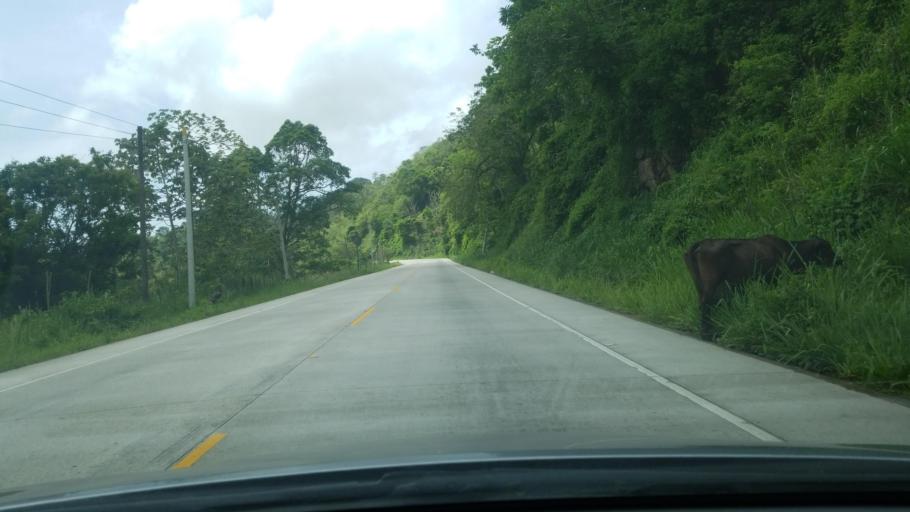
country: HN
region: Copan
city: Veracruz
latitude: 14.9210
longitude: -88.7627
